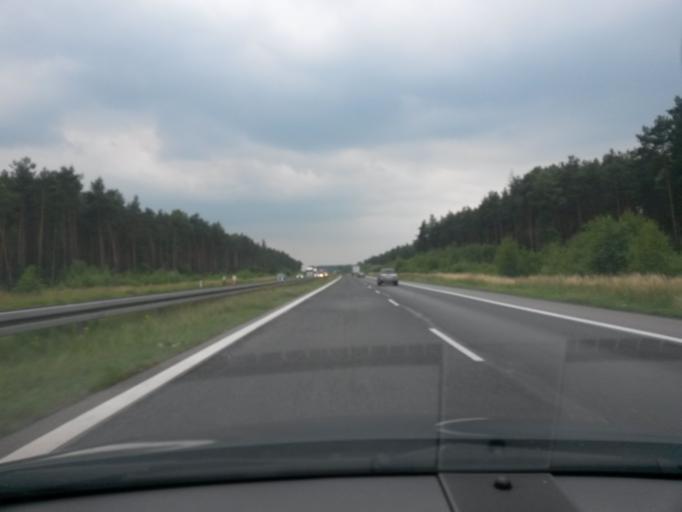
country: PL
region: Silesian Voivodeship
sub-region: Powiat czestochowski
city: Borowno
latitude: 51.0072
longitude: 19.2999
